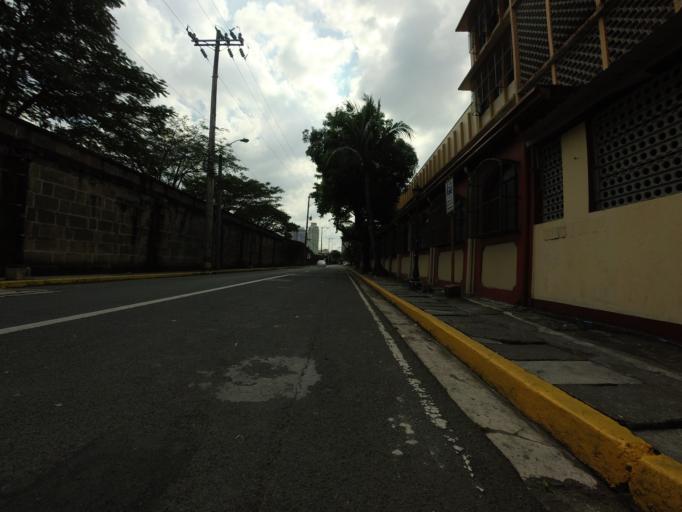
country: PH
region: Metro Manila
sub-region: City of Manila
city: Quiapo
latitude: 14.5893
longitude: 120.9788
